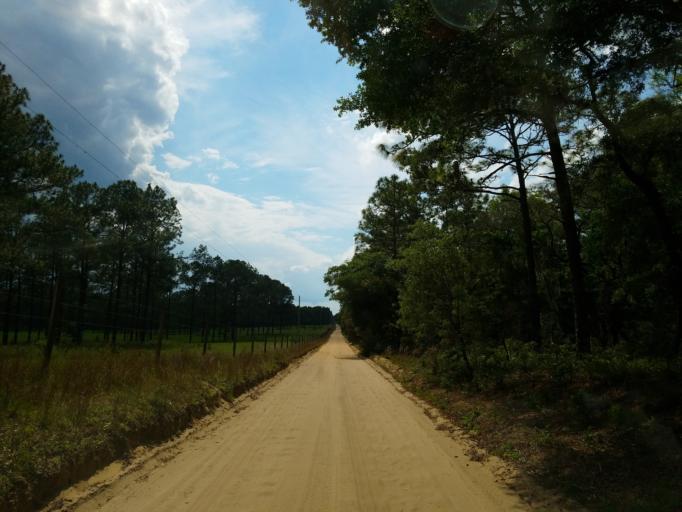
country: US
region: Florida
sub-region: Hernando County
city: Hill 'n Dale
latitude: 28.5576
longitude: -82.2624
